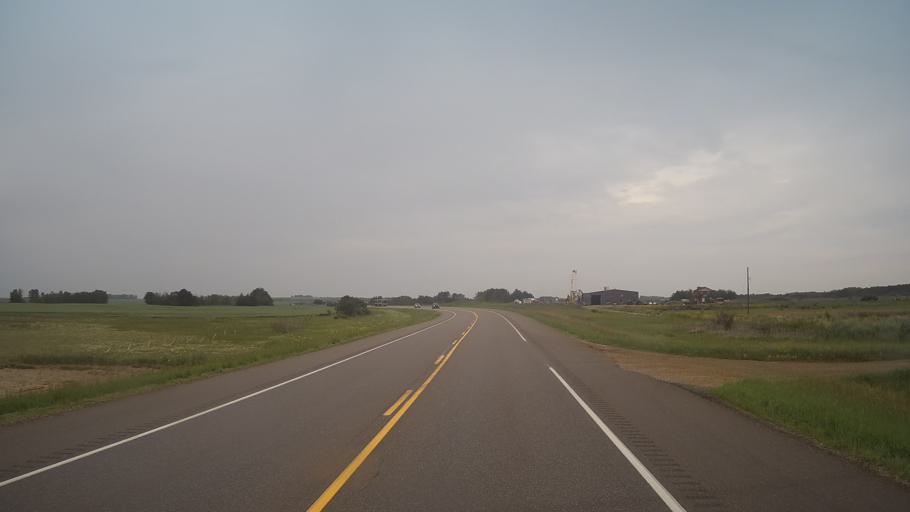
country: CA
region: Saskatchewan
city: Dalmeny
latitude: 52.1293
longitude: -106.8943
